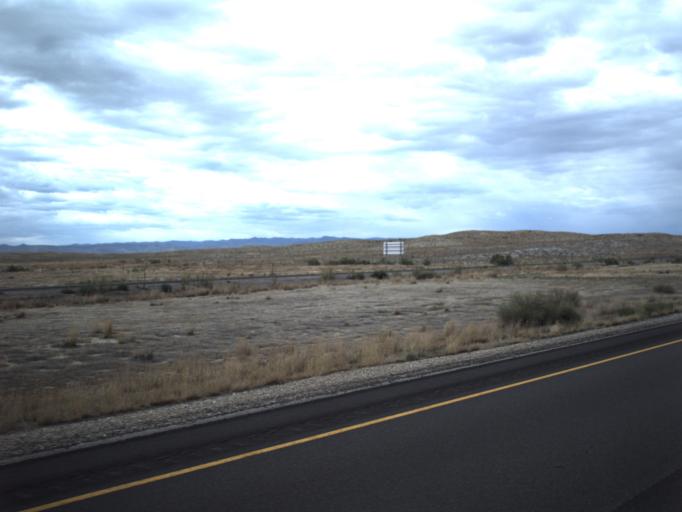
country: US
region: Colorado
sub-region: Mesa County
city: Loma
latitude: 39.1008
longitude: -109.2003
